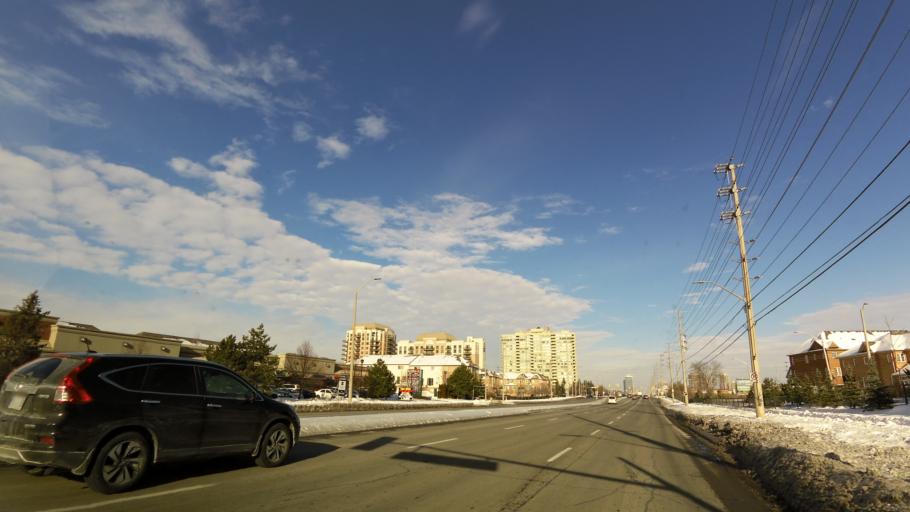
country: CA
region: Ontario
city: Mississauga
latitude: 43.5900
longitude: -79.6715
